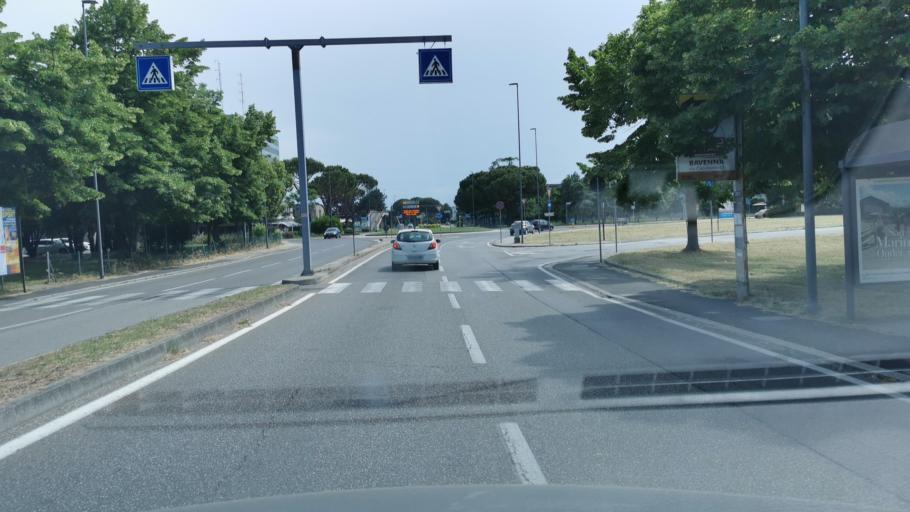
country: IT
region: Emilia-Romagna
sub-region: Provincia di Ravenna
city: Ravenna
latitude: 44.4258
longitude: 12.1827
